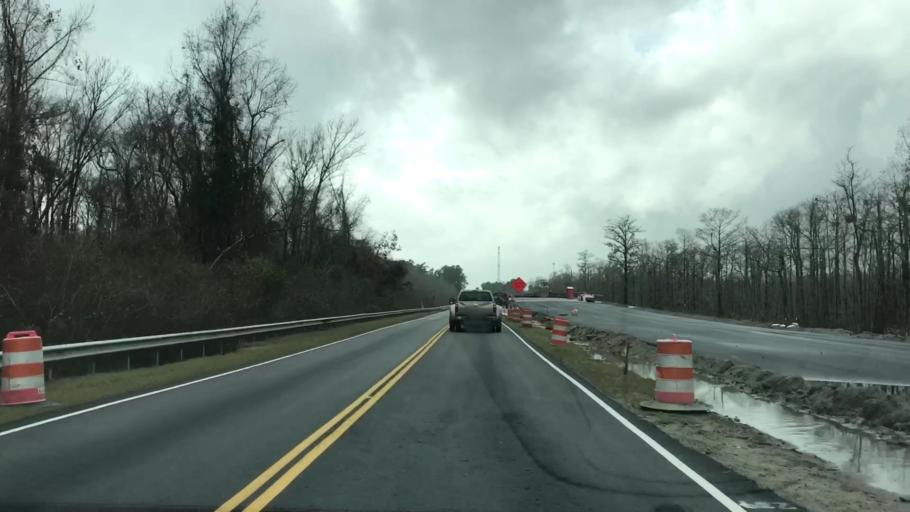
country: US
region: South Carolina
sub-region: Georgetown County
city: Murrells Inlet
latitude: 33.6576
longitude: -79.1586
